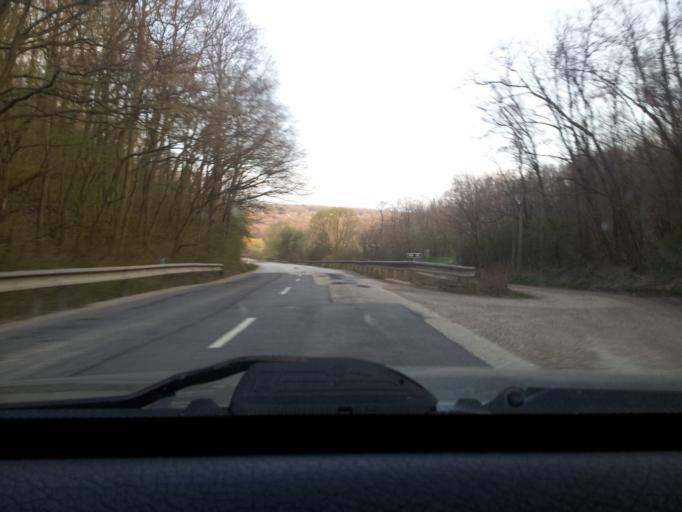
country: SK
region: Nitriansky
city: Tlmace
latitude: 48.2809
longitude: 18.4981
